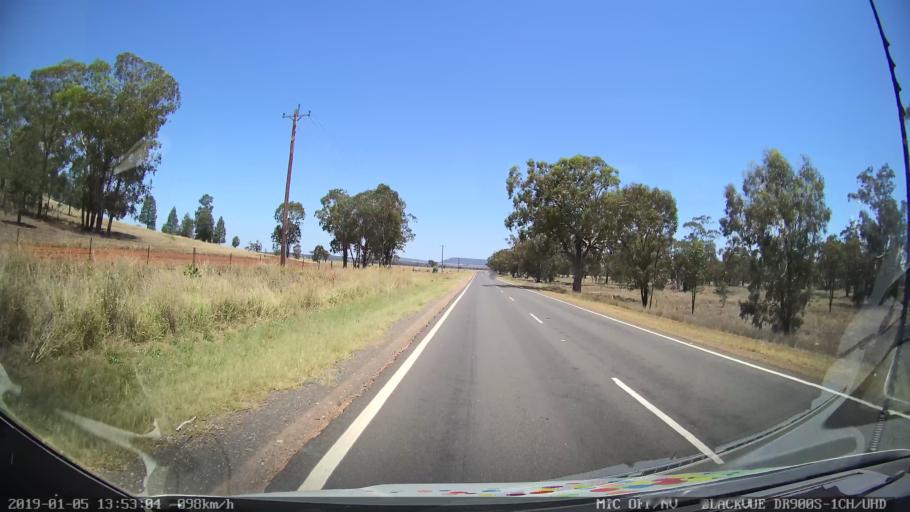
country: AU
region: New South Wales
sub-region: Gunnedah
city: Gunnedah
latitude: -31.0694
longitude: 150.2770
